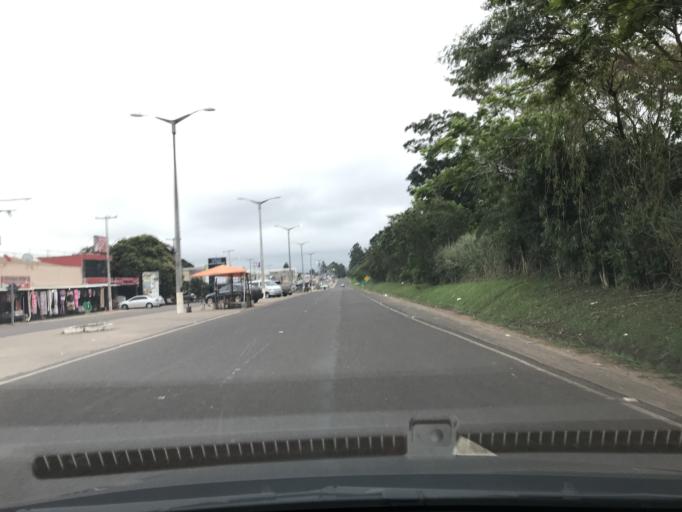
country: PY
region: Canindeyu
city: Salto del Guaira
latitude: -24.0499
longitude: -54.3061
